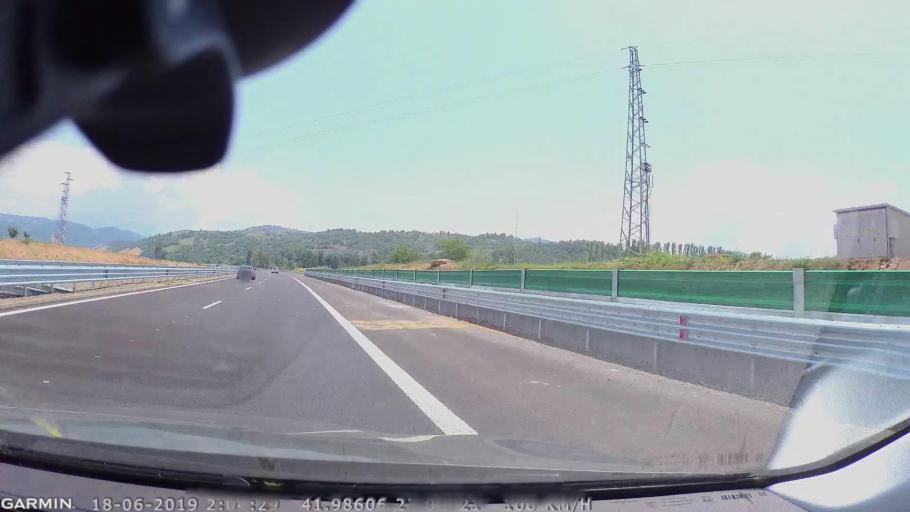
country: BG
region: Blagoevgrad
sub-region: Obshtina Blagoevgrad
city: Blagoevgrad
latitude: 41.9851
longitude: 23.0582
